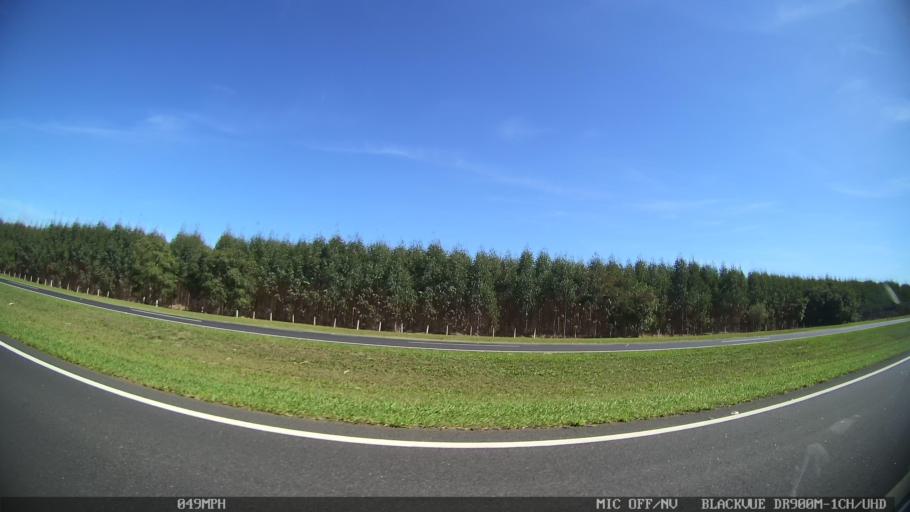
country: BR
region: Sao Paulo
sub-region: Sao Simao
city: Sao Simao
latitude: -21.5651
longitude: -47.6332
